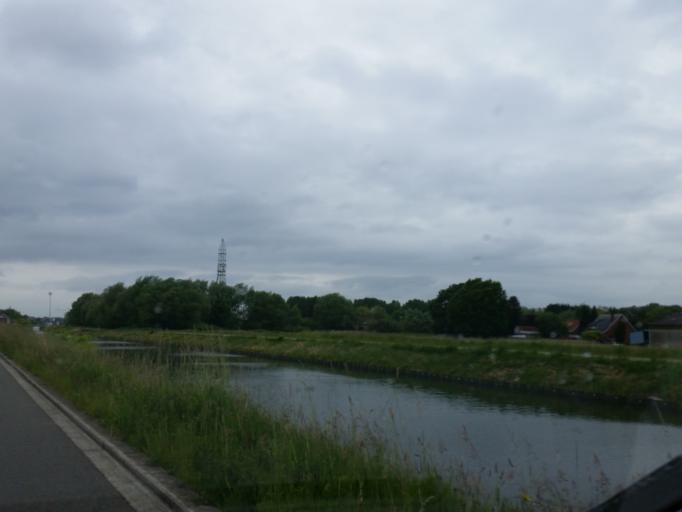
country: BE
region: Flanders
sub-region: Provincie Antwerpen
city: Mechelen
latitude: 51.0064
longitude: 4.4972
